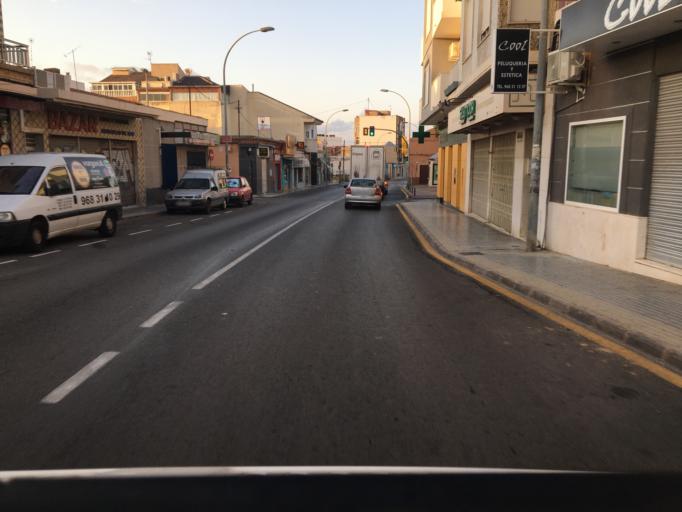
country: ES
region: Murcia
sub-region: Murcia
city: Cartagena
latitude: 37.6245
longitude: -0.9888
